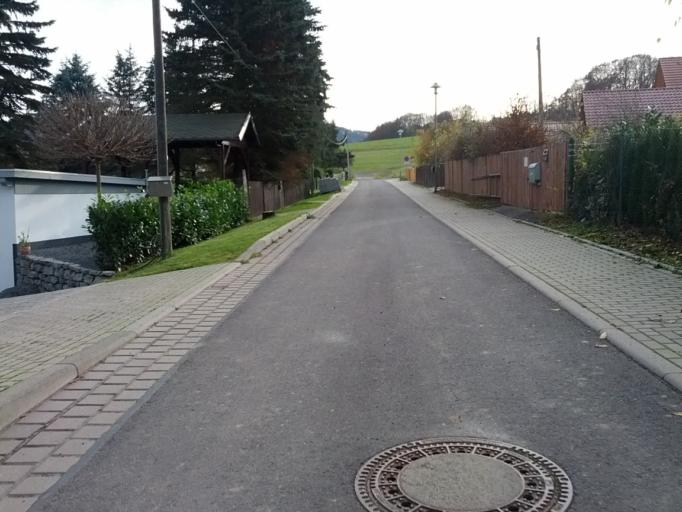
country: DE
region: Thuringia
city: Ruhla
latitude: 50.9351
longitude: 10.3513
